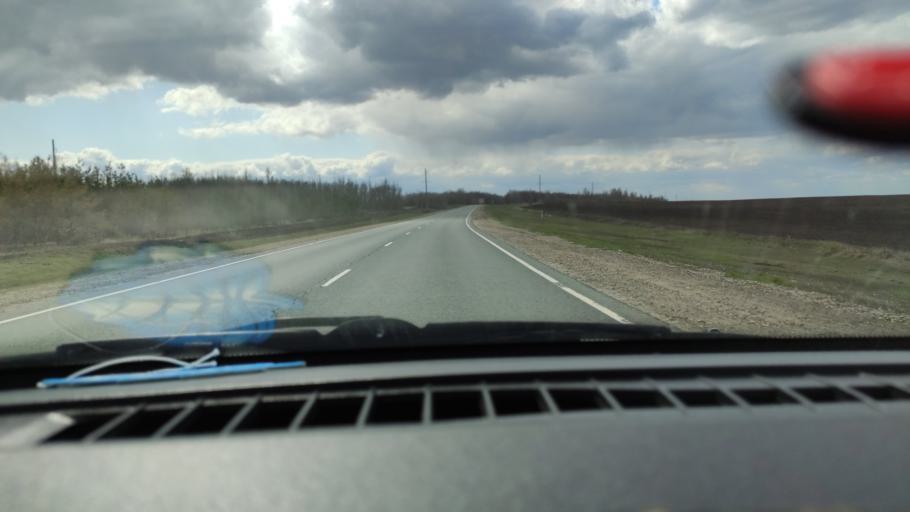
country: RU
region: Saratov
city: Alekseyevka
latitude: 52.2726
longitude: 47.9298
